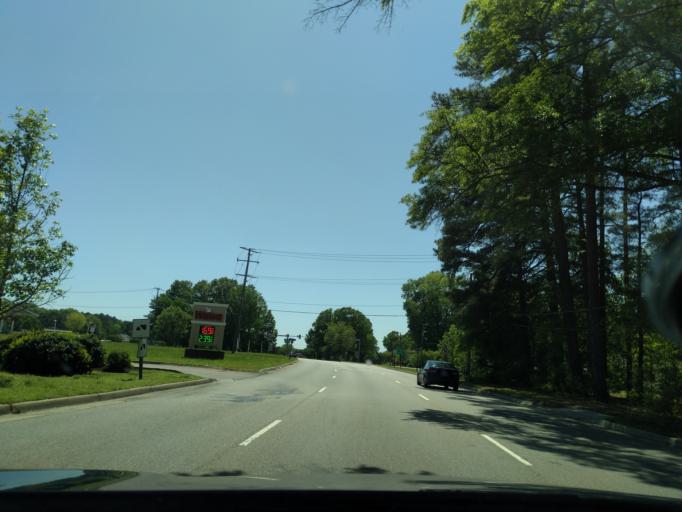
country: US
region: Virginia
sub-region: Prince George County
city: Fort Lee
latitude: 37.2724
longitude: -77.3172
